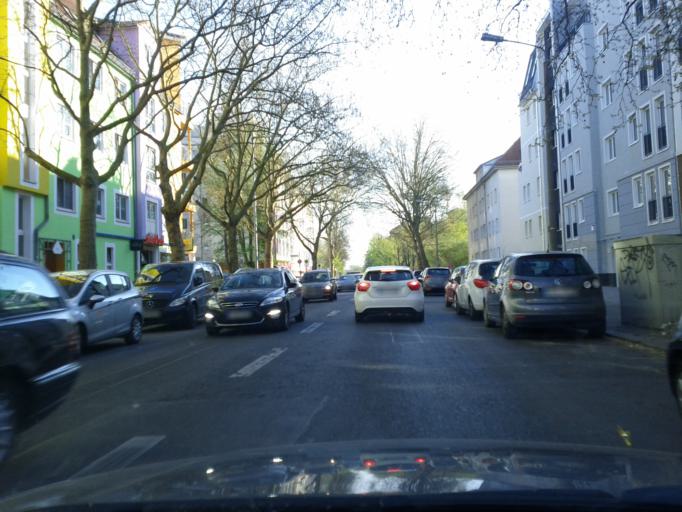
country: DE
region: Berlin
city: Wilhelmsruh
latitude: 52.5847
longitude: 13.3661
